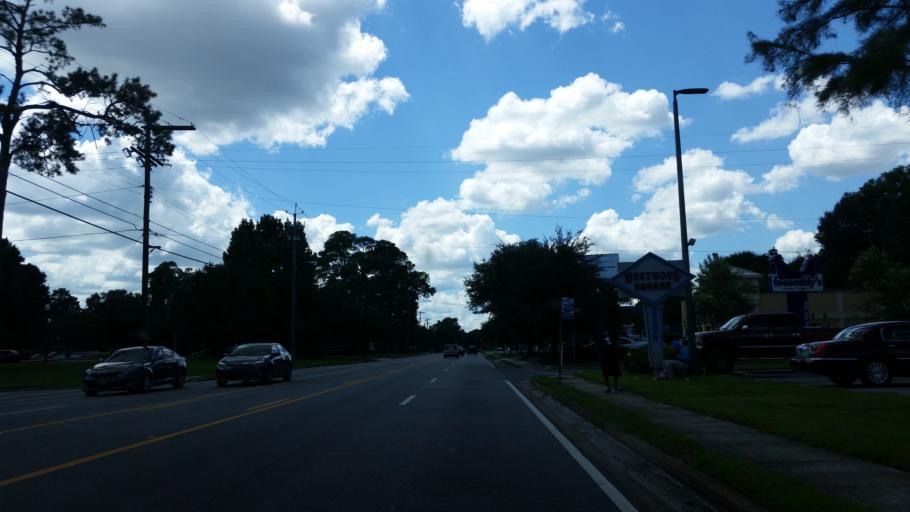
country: US
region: Alabama
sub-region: Mobile County
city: Mobile
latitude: 30.6765
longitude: -88.0933
